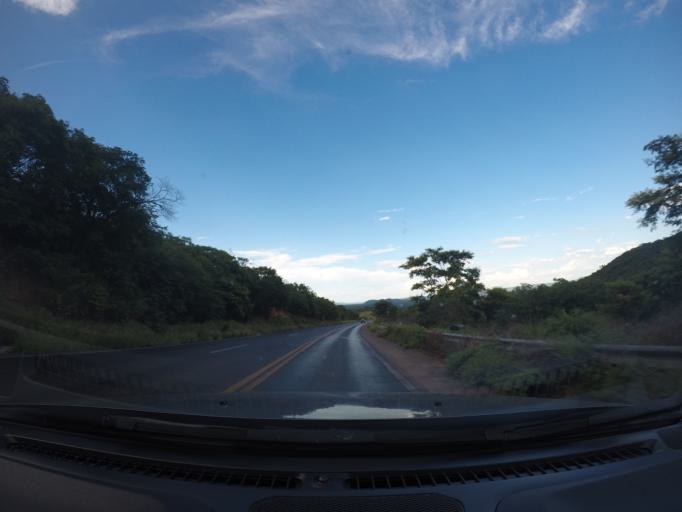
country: BR
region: Bahia
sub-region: Ibotirama
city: Ibotirama
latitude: -12.1340
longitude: -43.3506
